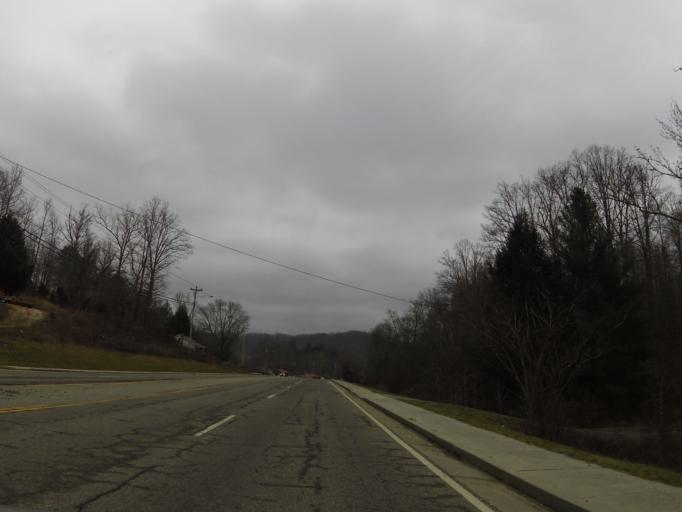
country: US
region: Tennessee
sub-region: Scott County
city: Huntsville
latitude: 36.4159
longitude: -84.5089
